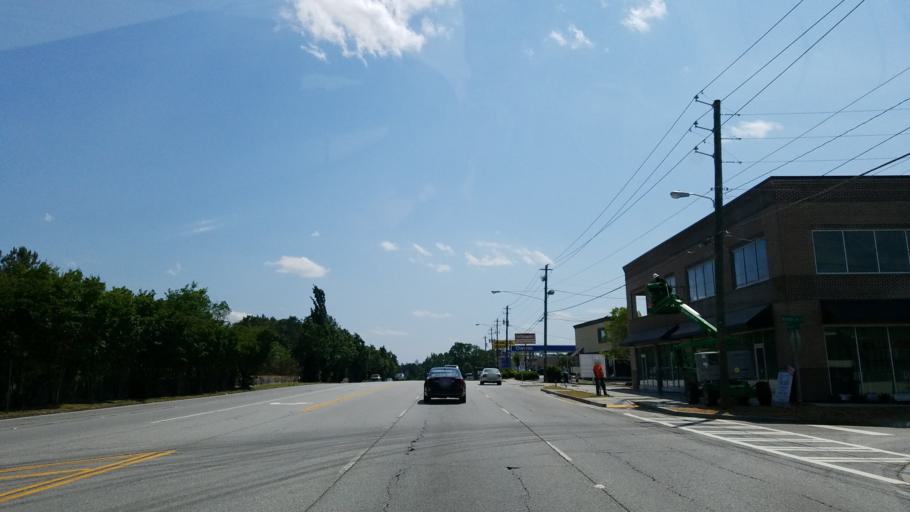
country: US
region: Georgia
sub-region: DeKalb County
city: North Atlanta
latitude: 33.8678
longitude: -84.3353
